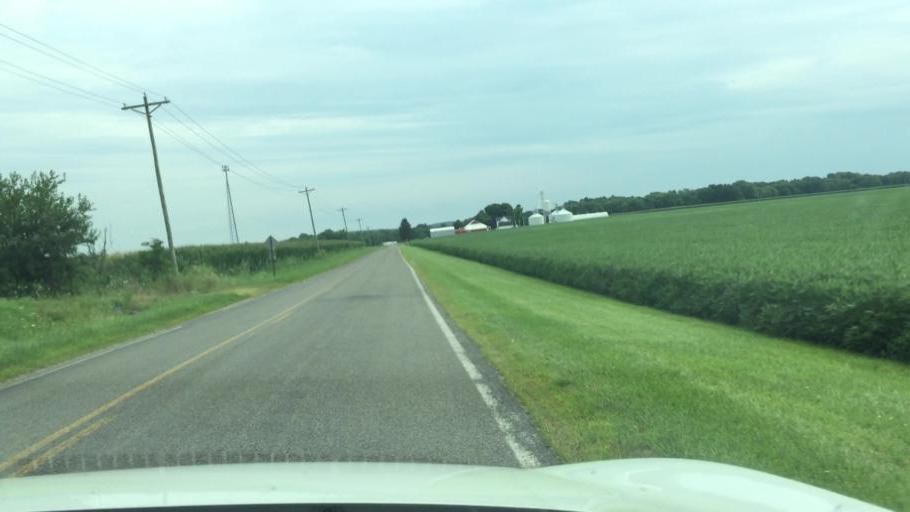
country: US
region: Ohio
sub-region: Champaign County
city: Mechanicsburg
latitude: 40.0384
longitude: -83.6561
